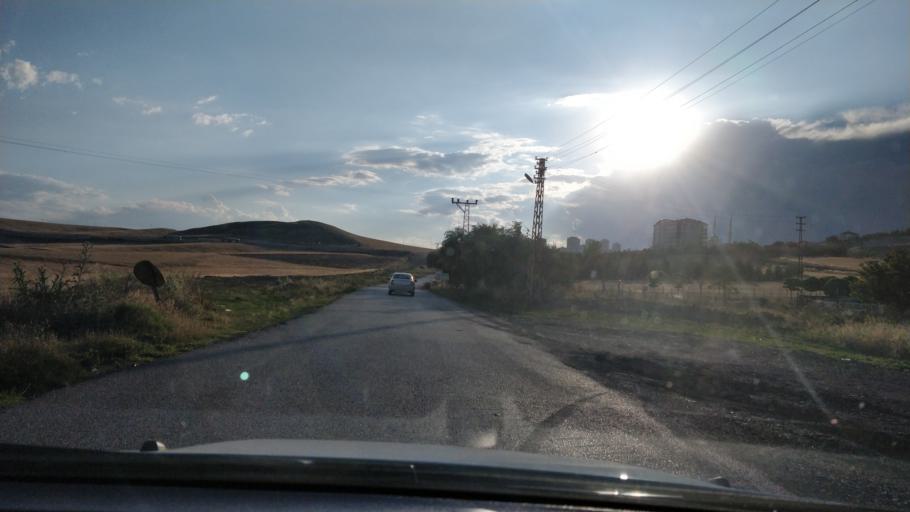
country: TR
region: Ankara
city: Etimesgut
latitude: 39.8269
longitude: 32.5618
